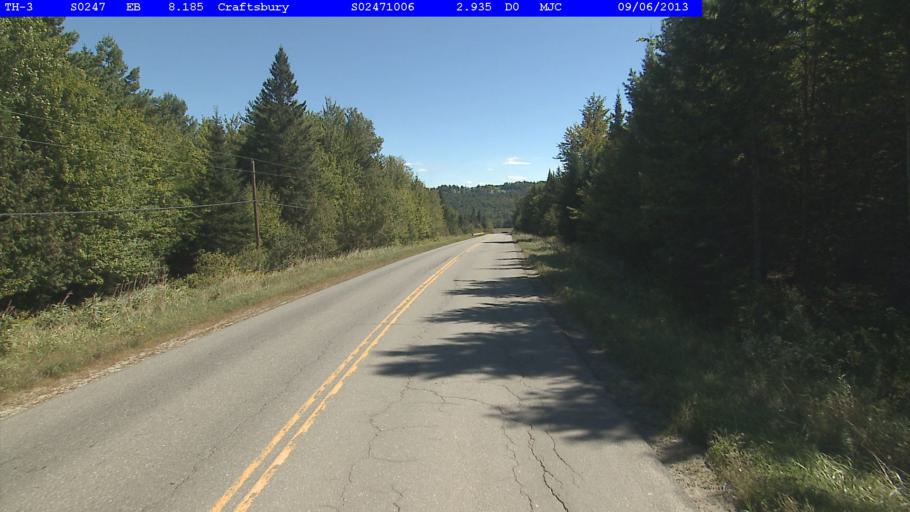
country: US
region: Vermont
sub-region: Caledonia County
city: Hardwick
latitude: 44.6525
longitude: -72.4135
